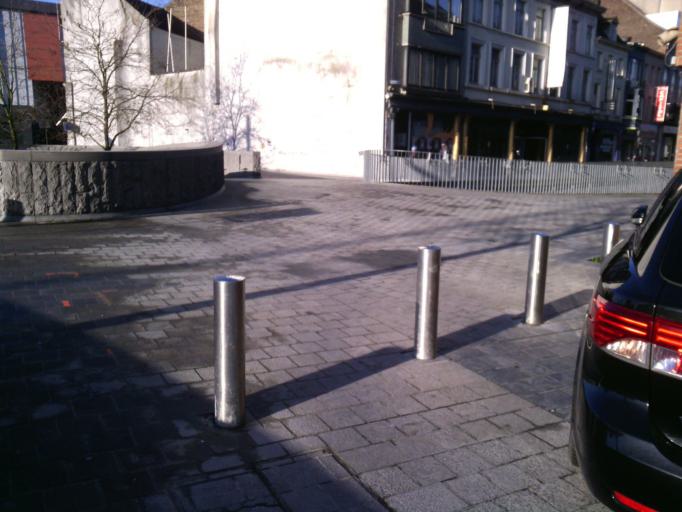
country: BE
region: Flanders
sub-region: Provincie West-Vlaanderen
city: Kortrijk
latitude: 50.8247
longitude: 3.2682
